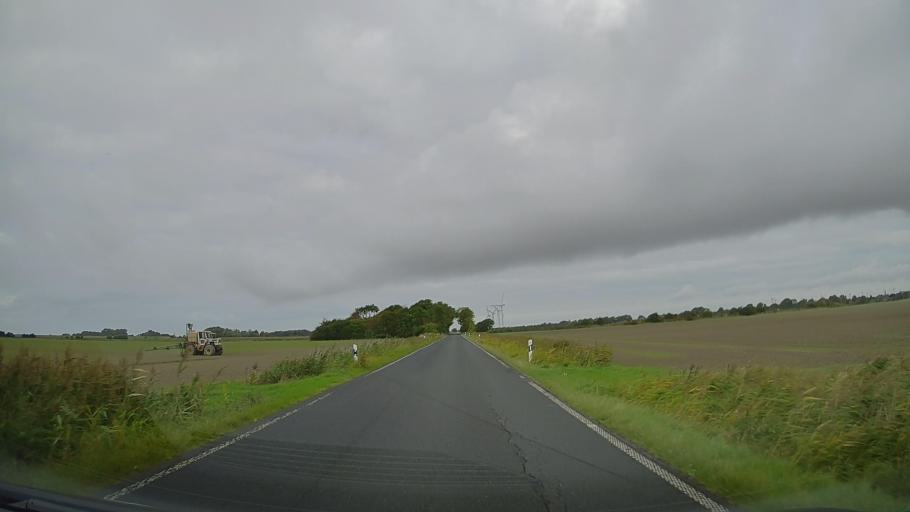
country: DE
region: Schleswig-Holstein
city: Galmsbull
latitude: 54.7592
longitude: 8.7238
